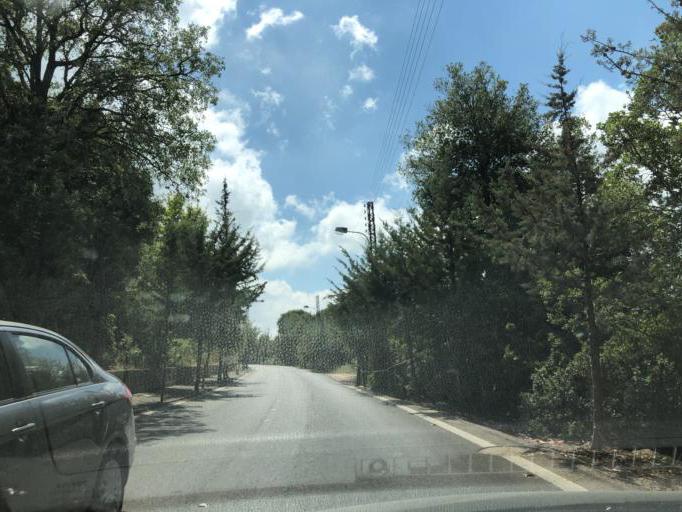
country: LB
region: Mont-Liban
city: Beit ed Dine
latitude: 33.6967
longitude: 35.5862
